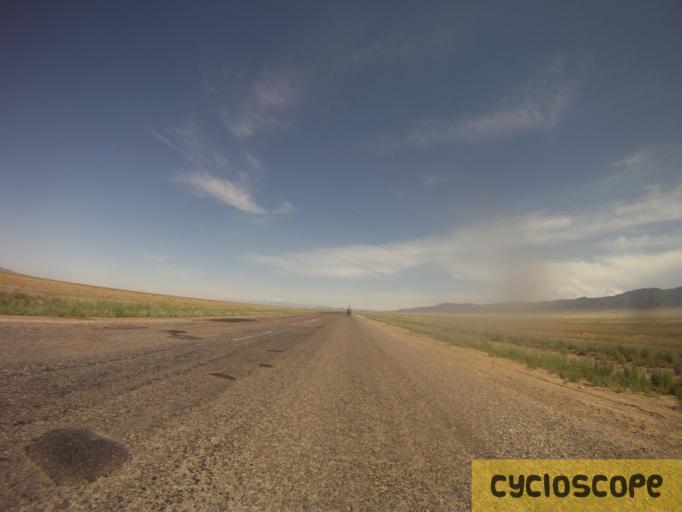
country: KZ
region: Almaty Oblysy
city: Kegen
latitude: 43.4047
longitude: 78.7907
